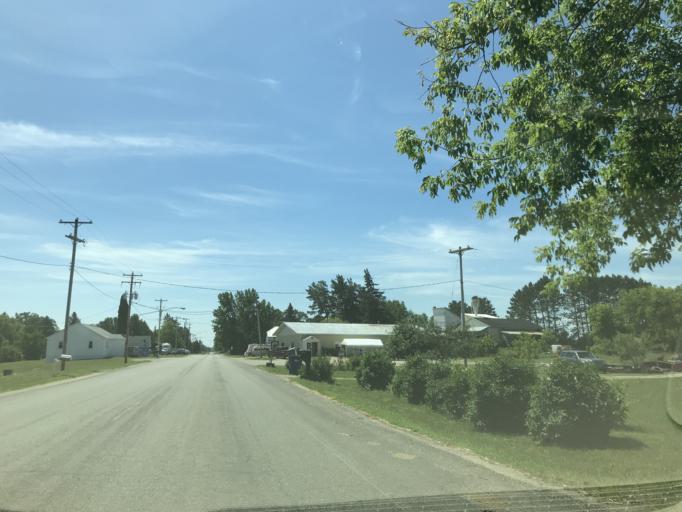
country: US
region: Michigan
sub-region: Roscommon County
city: Houghton Lake
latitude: 44.3323
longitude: -84.9446
